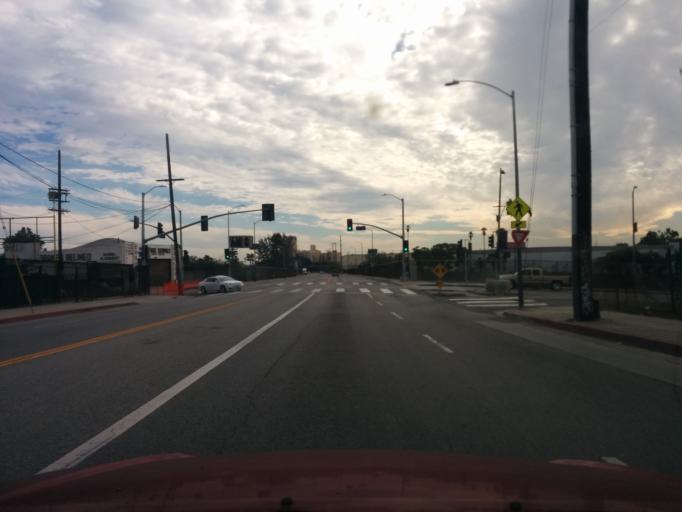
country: US
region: California
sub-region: Los Angeles County
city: Boyle Heights
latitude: 34.0341
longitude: -118.2195
